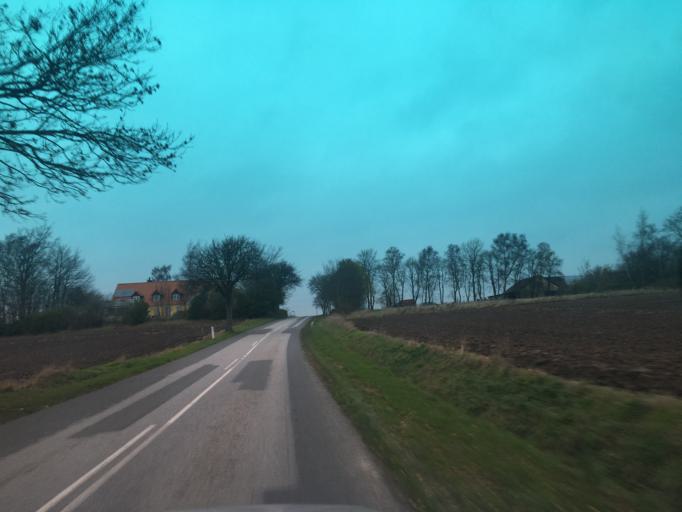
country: DK
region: Zealand
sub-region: Slagelse Kommune
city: Skaelskor
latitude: 55.2458
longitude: 11.4230
